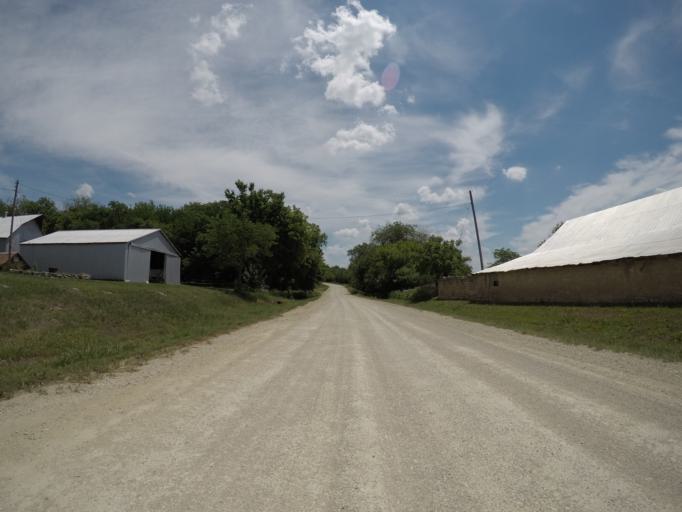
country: US
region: Kansas
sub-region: Wabaunsee County
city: Alma
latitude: 38.9176
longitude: -96.2180
